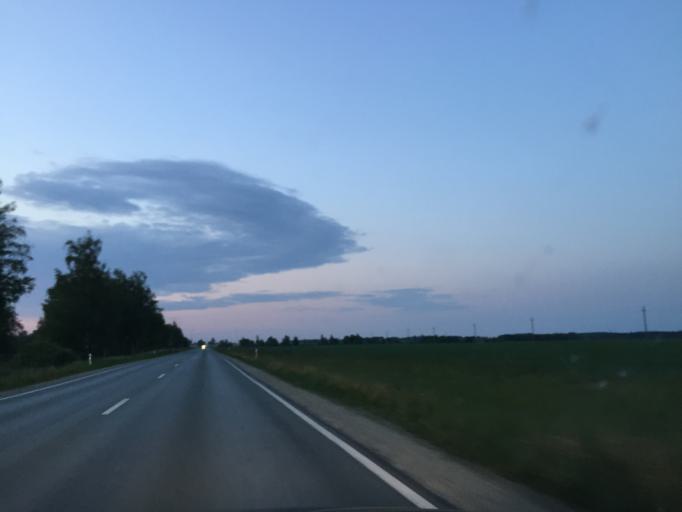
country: LT
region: Siauliu apskritis
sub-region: Joniskis
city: Joniskis
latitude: 56.1152
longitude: 23.4937
